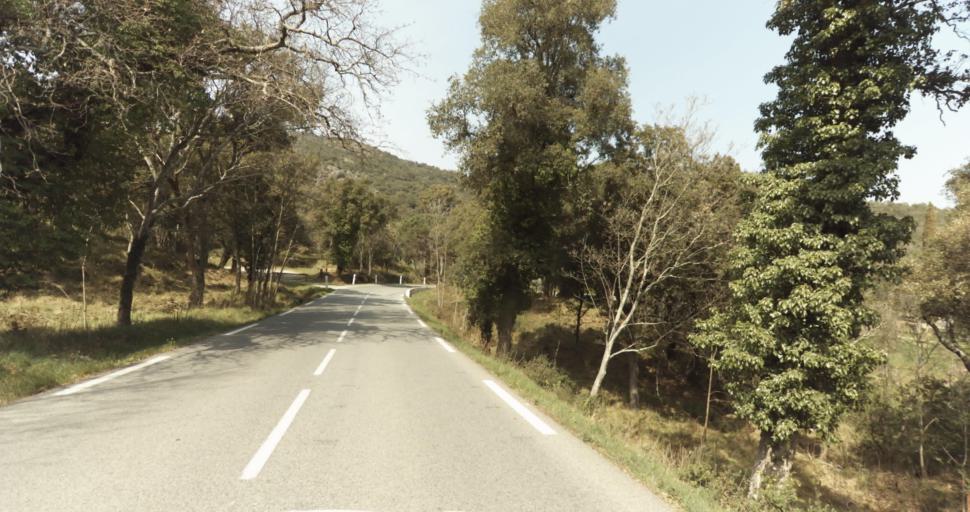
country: FR
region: Provence-Alpes-Cote d'Azur
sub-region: Departement du Var
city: Bormes-les-Mimosas
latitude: 43.1779
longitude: 6.3362
